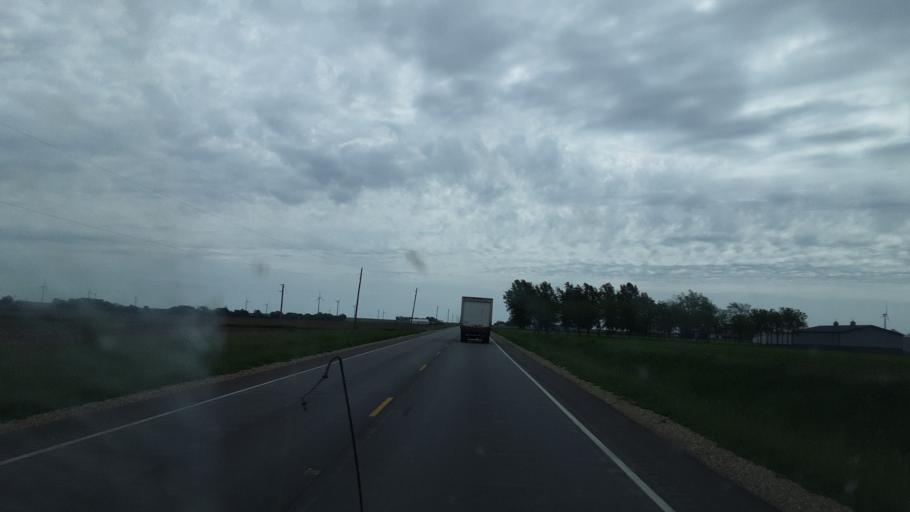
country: US
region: Illinois
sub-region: Tazewell County
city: Richmond
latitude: 40.3086
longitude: -89.4406
